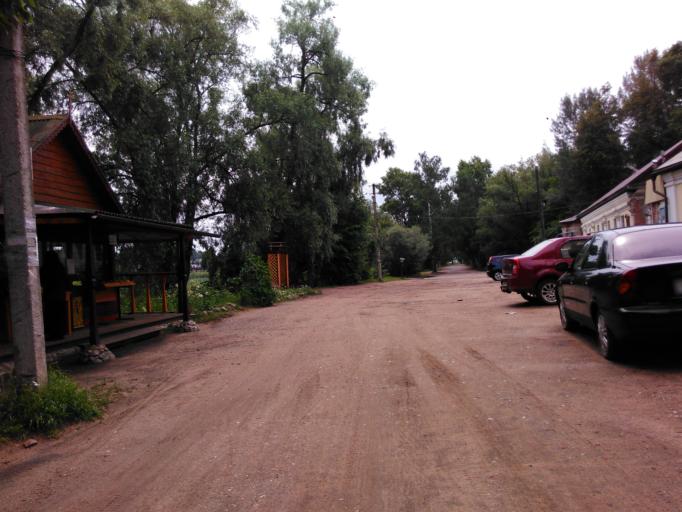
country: RU
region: Tverskaya
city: Ostashkov
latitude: 57.1675
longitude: 33.0943
